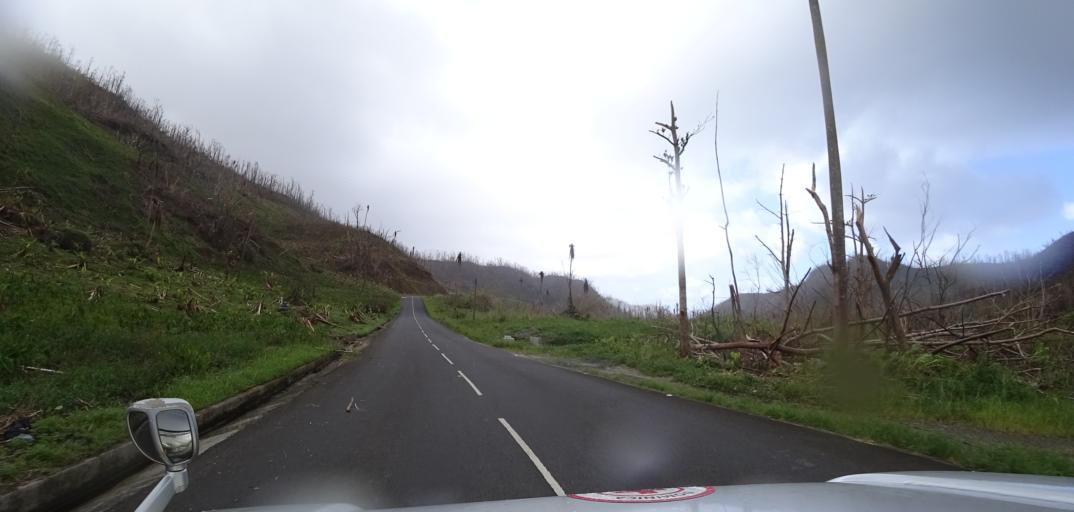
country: DM
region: Saint Andrew
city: Marigot
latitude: 15.5060
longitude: -61.2787
